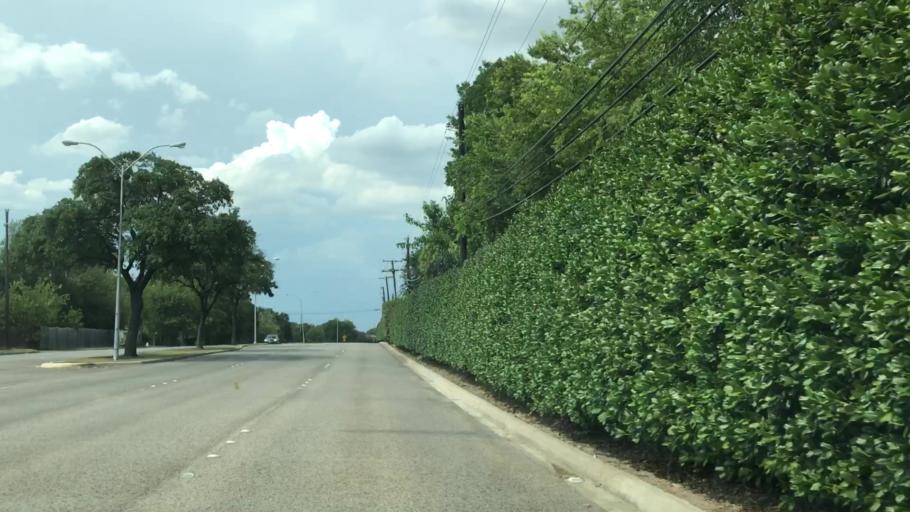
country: US
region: Texas
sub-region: Dallas County
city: Carrollton
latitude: 32.9411
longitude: -96.8731
